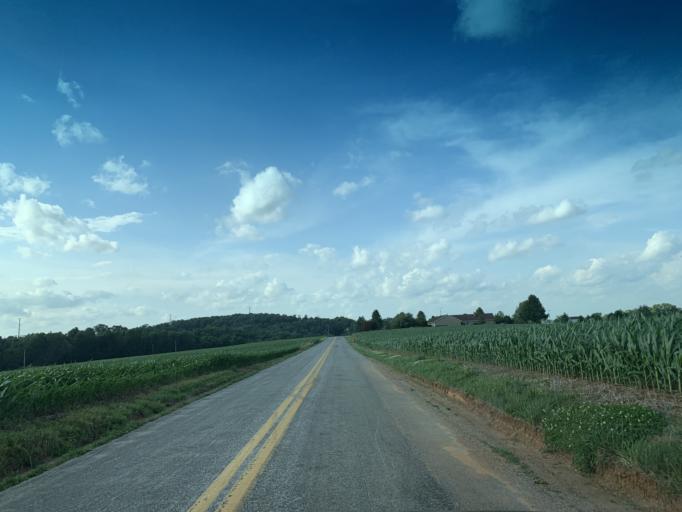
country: US
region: Pennsylvania
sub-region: York County
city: Stewartstown
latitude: 39.7441
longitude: -76.5427
